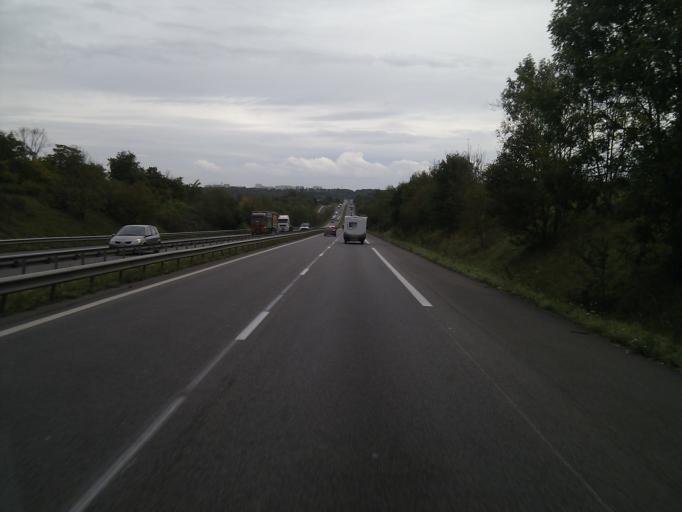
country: FR
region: Lorraine
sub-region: Departement de Meurthe-et-Moselle
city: Liverdun
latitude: 48.6935
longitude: 6.0814
